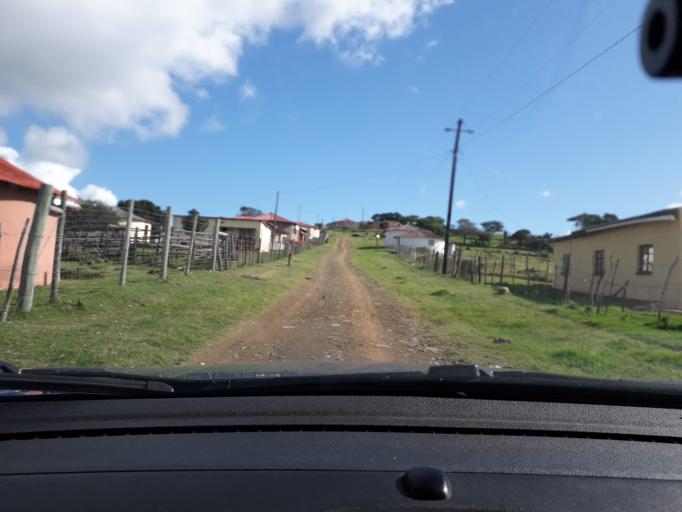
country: ZA
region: Eastern Cape
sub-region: Buffalo City Metropolitan Municipality
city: Bhisho
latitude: -33.1137
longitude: 27.4321
